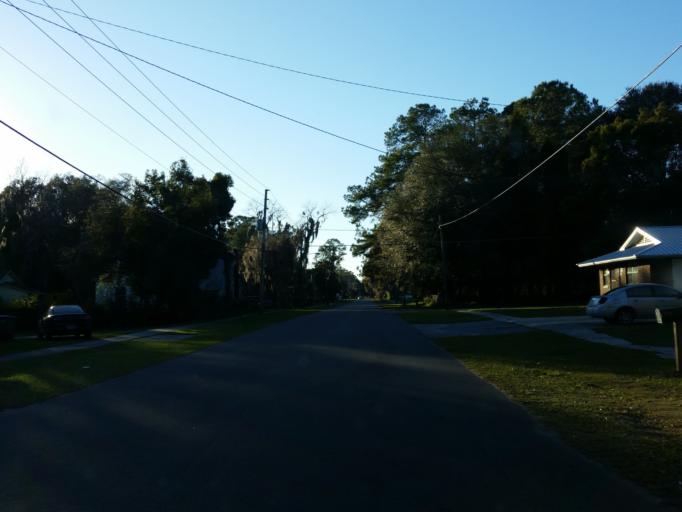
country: US
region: Florida
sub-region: Hamilton County
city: Jasper
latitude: 30.5209
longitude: -82.9498
